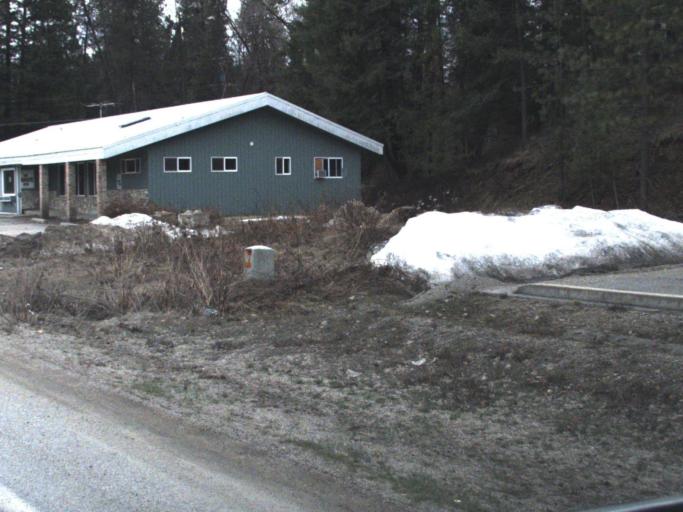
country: US
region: Washington
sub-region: Pend Oreille County
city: Newport
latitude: 48.1861
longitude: -117.0483
